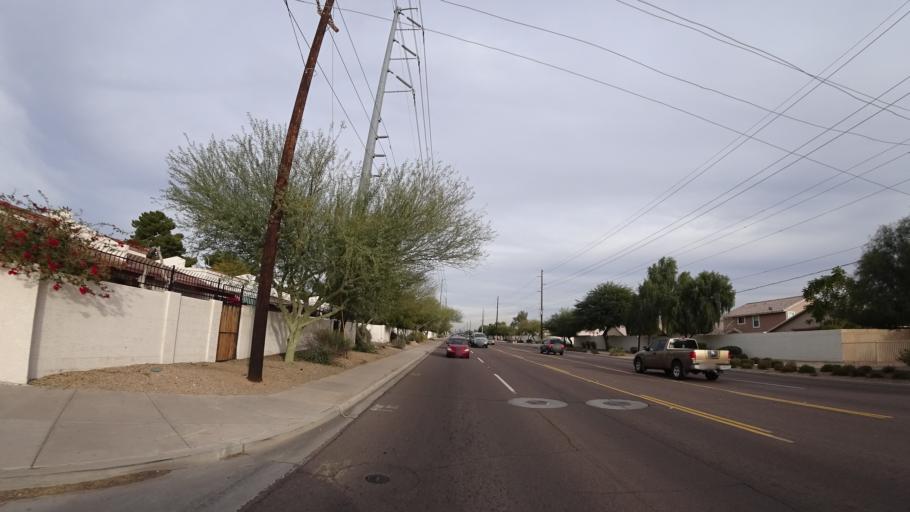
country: US
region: Arizona
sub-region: Maricopa County
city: Peoria
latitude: 33.5672
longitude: -112.2070
